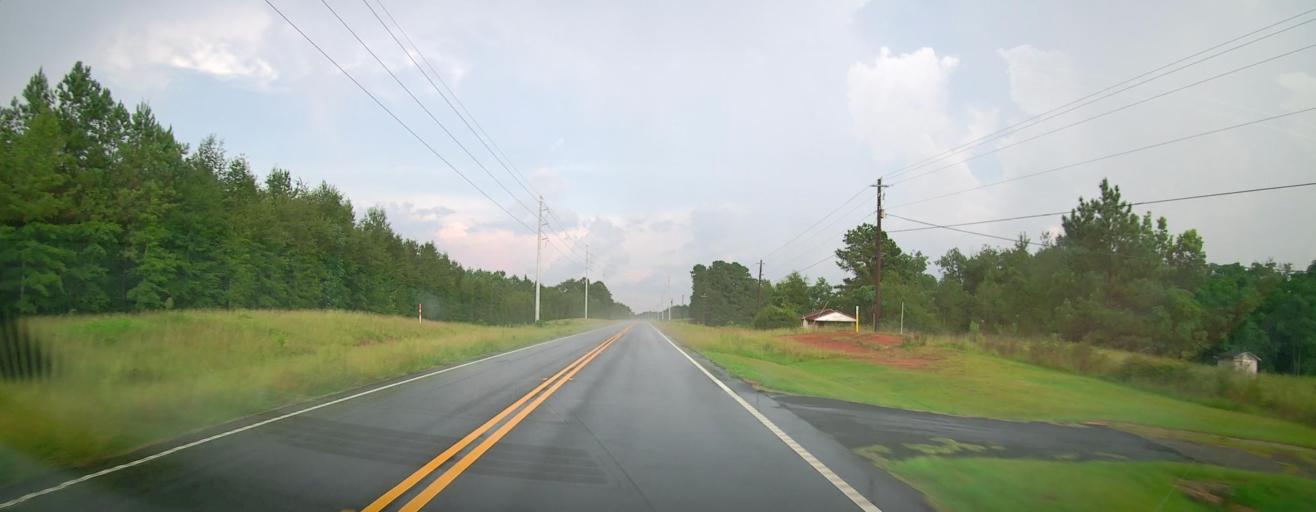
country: US
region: Georgia
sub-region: Twiggs County
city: Jeffersonville
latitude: 32.5779
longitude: -83.2075
